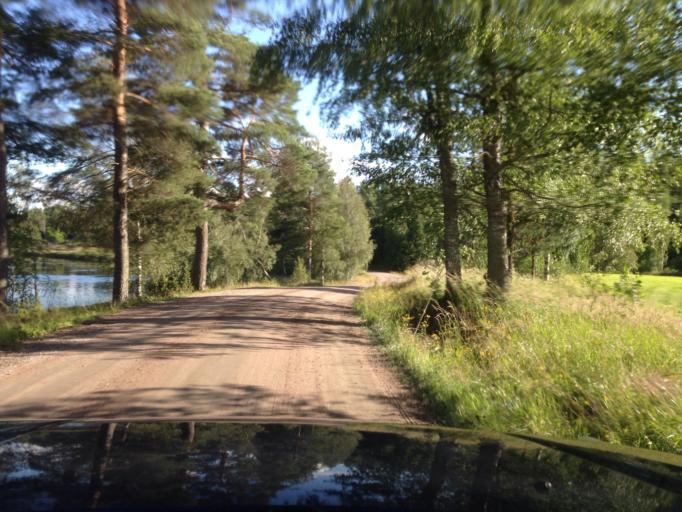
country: SE
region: Dalarna
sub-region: Ludvika Kommun
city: Abborrberget
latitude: 60.2745
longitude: 14.7287
